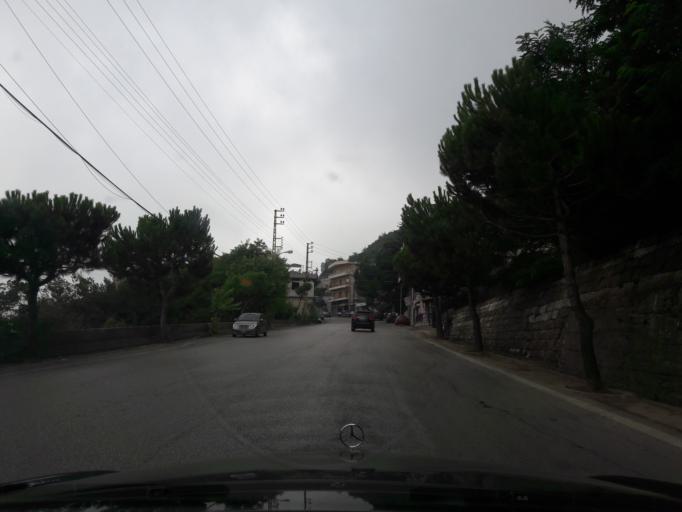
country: LB
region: Mont-Liban
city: Djounie
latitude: 33.9175
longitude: 35.6672
